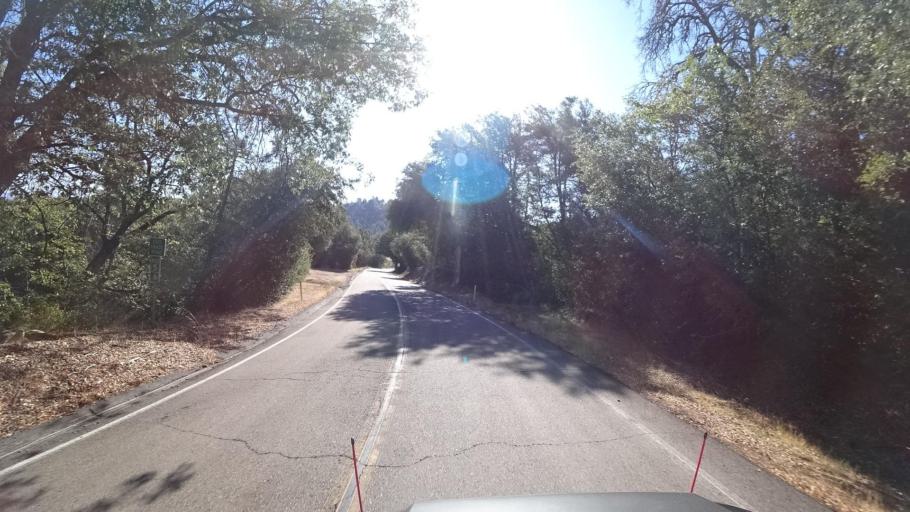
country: US
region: California
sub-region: Riverside County
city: Aguanga
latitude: 33.2847
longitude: -116.7932
